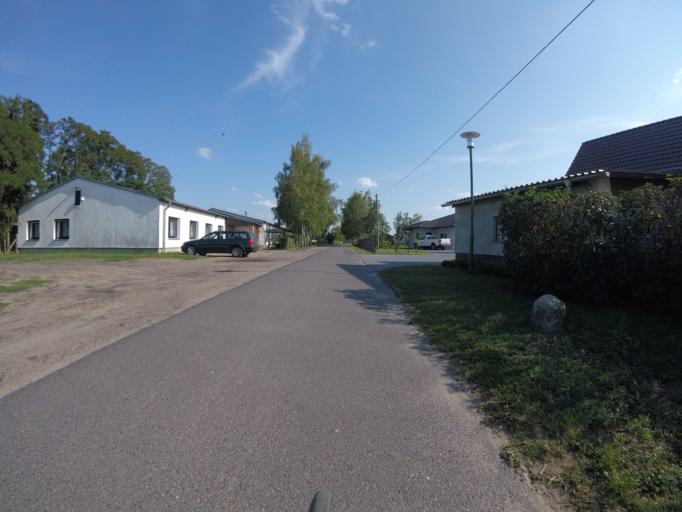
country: DE
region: Brandenburg
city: Bliesdorf
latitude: 52.6925
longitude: 14.1582
